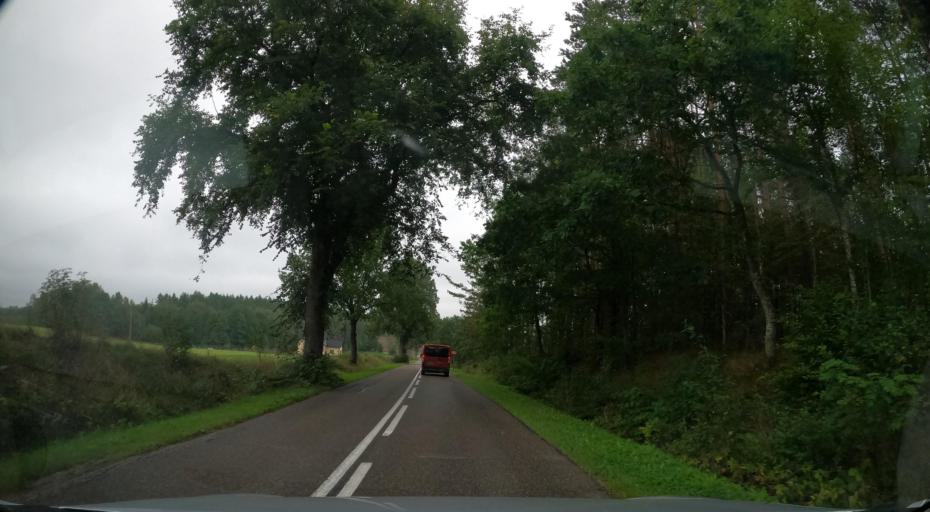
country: PL
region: Pomeranian Voivodeship
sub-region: Powiat wejherowski
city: Luzino
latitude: 54.4899
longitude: 18.1201
